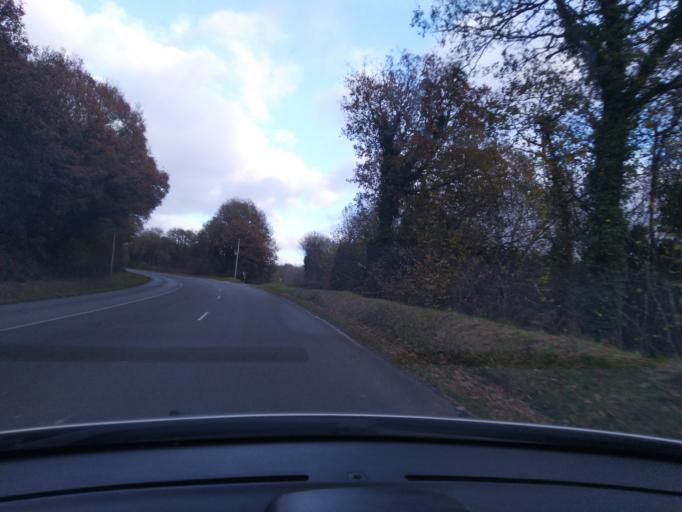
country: FR
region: Brittany
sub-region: Departement du Finistere
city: Guerlesquin
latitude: 48.5606
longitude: -3.6281
